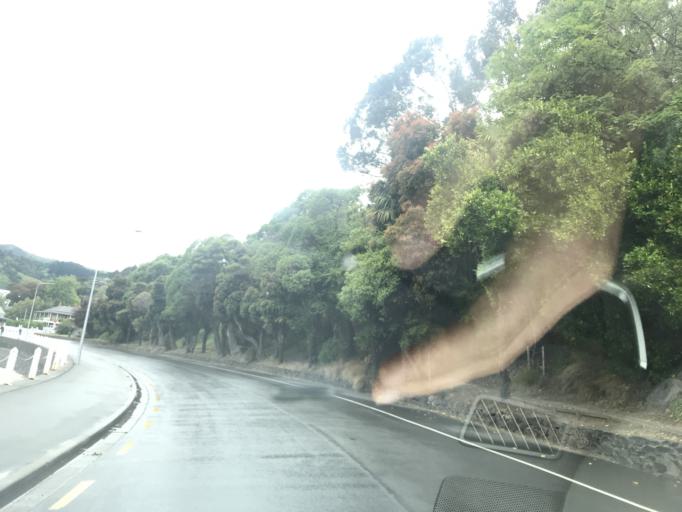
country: NZ
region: Canterbury
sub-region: Christchurch City
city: Christchurch
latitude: -43.8083
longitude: 172.9650
